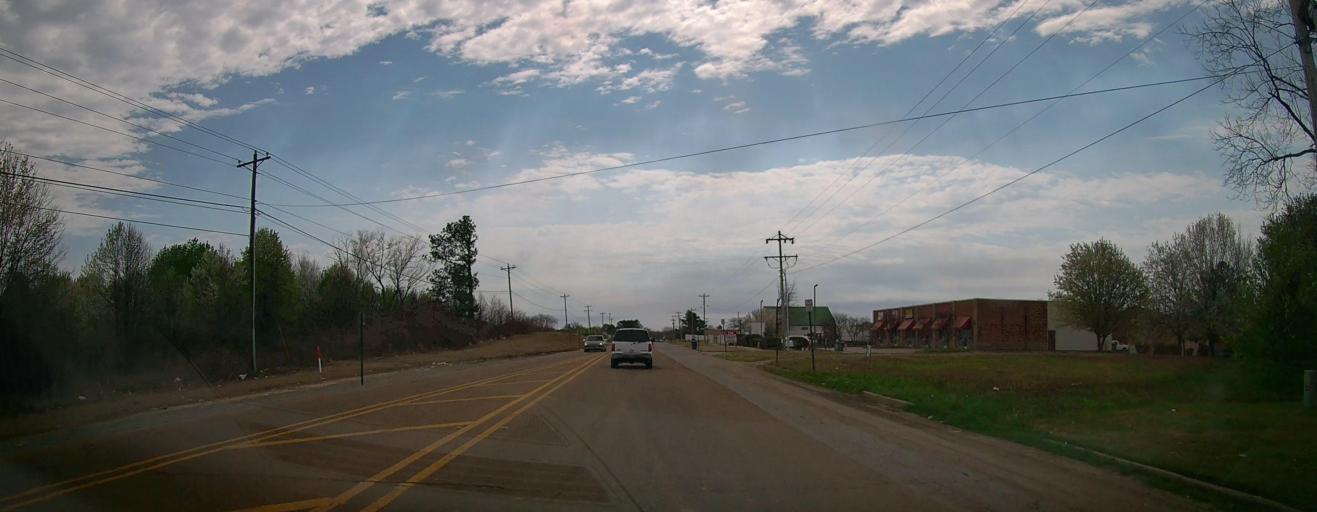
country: US
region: Mississippi
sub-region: De Soto County
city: Olive Branch
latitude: 34.9317
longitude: -89.7939
